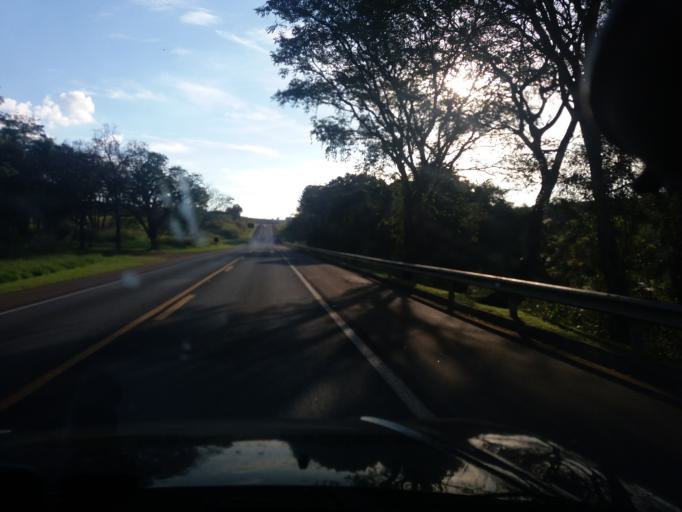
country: BR
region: Sao Paulo
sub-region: Buri
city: Buri
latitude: -23.9300
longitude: -48.6471
